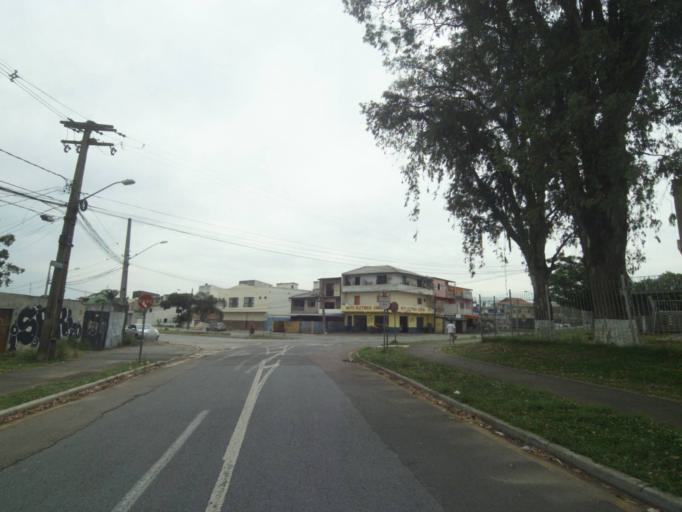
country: BR
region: Parana
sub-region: Curitiba
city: Curitiba
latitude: -25.5130
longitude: -49.3324
